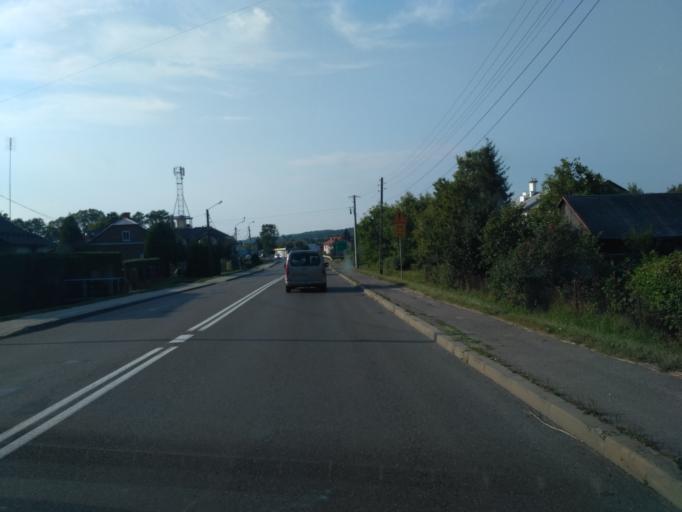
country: PL
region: Subcarpathian Voivodeship
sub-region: Powiat brzozowski
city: Grabownica Starzenska
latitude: 49.6556
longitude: 22.0794
